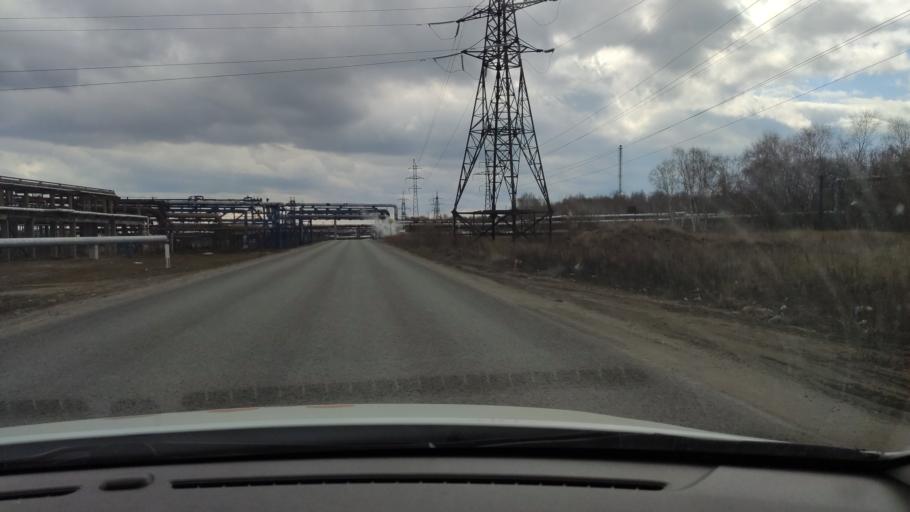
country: RU
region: Tatarstan
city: Staroye Arakchino
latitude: 55.8712
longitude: 48.9740
